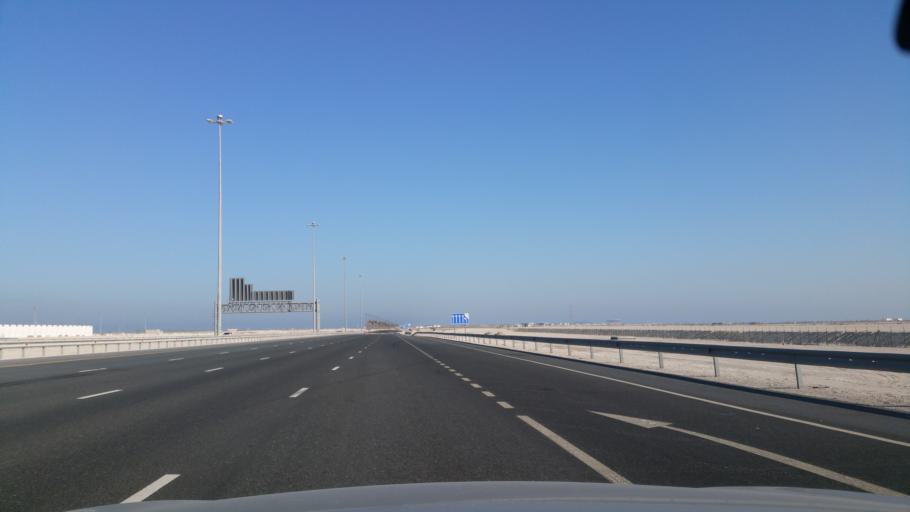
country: QA
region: Al Wakrah
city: Umm Sa'id
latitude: 25.0618
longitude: 51.5830
